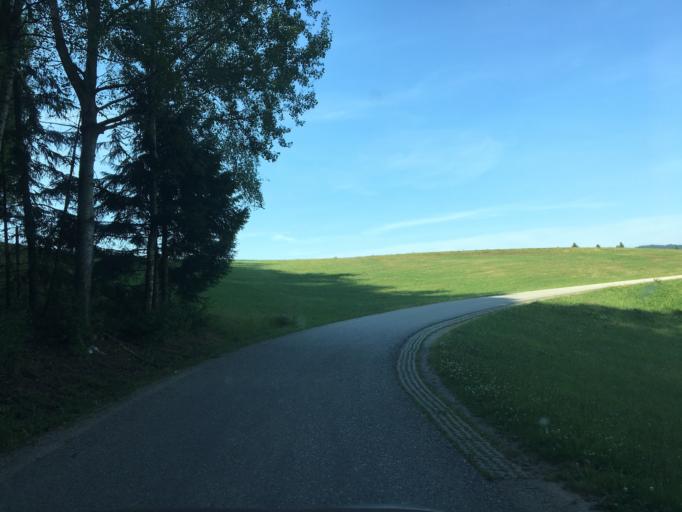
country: AT
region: Upper Austria
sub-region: Politischer Bezirk Urfahr-Umgebung
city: Oberneukirchen
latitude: 48.4388
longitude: 14.1752
